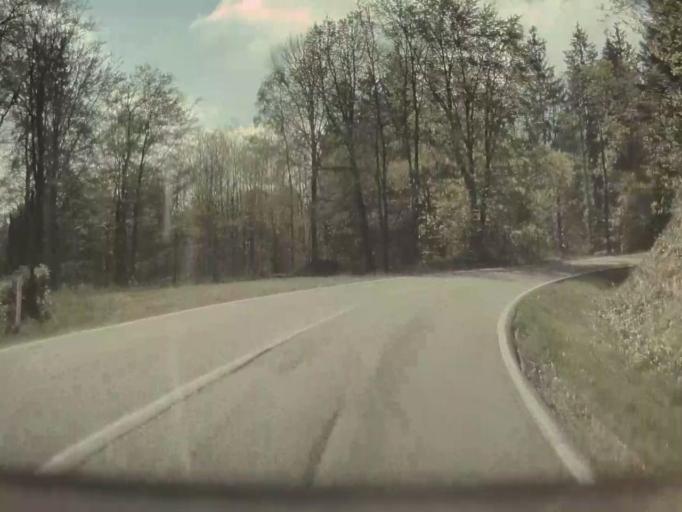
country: BE
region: Wallonia
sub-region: Province du Luxembourg
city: Tellin
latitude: 50.0195
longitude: 5.2051
